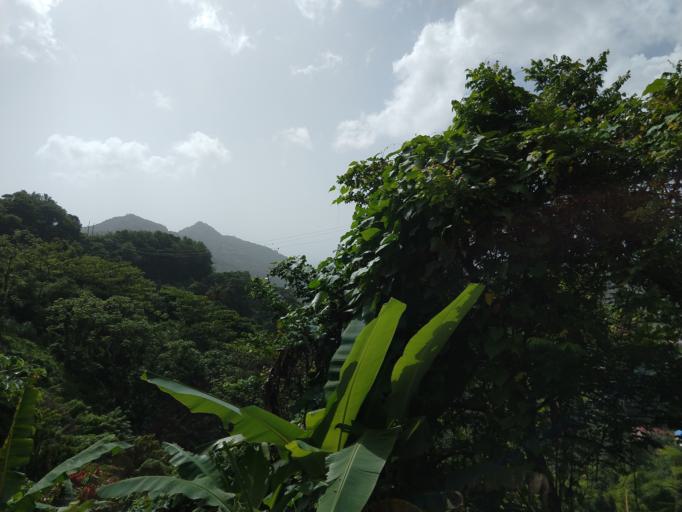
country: GD
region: Saint George
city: Saint George's
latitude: 12.0802
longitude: -61.7174
